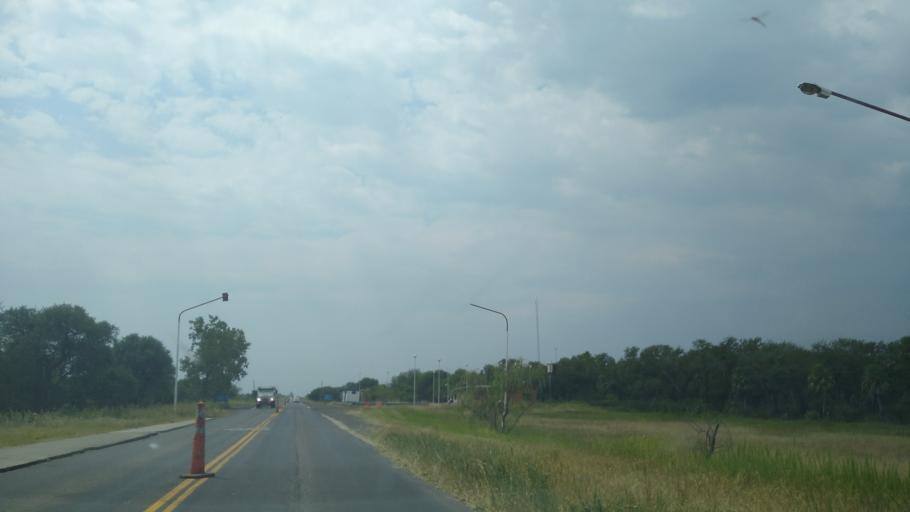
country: AR
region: Chaco
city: Margarita Belen
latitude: -27.1184
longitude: -58.9708
